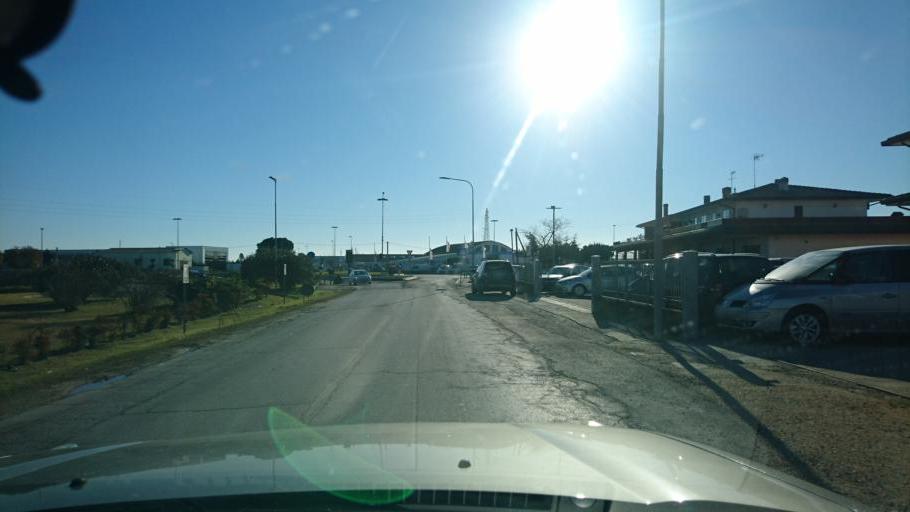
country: IT
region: Veneto
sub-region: Provincia di Rovigo
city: Porto Viro
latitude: 45.0323
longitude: 12.2332
